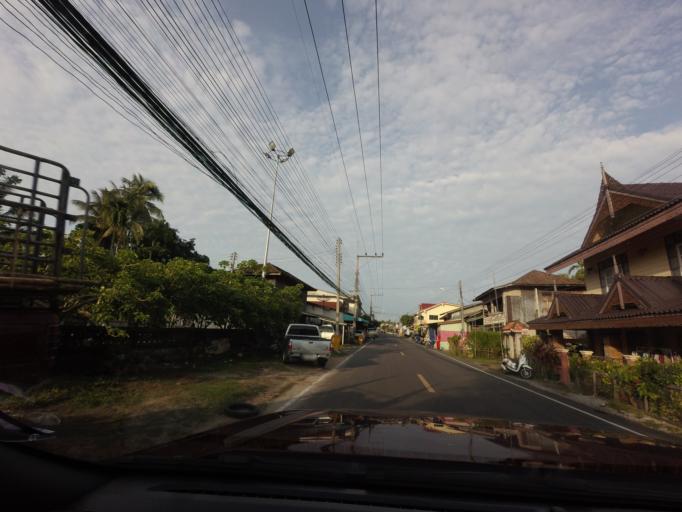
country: TH
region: Pattani
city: Yaring
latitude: 6.8689
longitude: 101.3408
